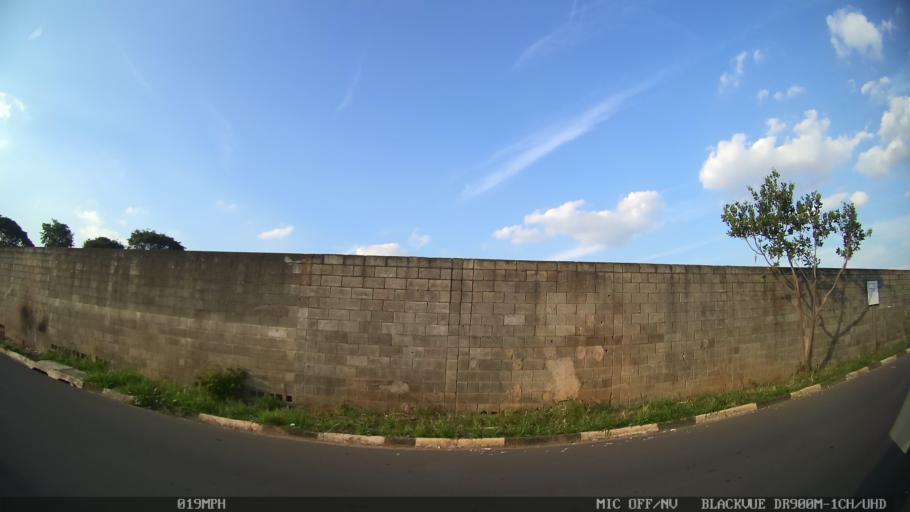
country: BR
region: Sao Paulo
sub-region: Hortolandia
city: Hortolandia
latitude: -22.8819
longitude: -47.1620
